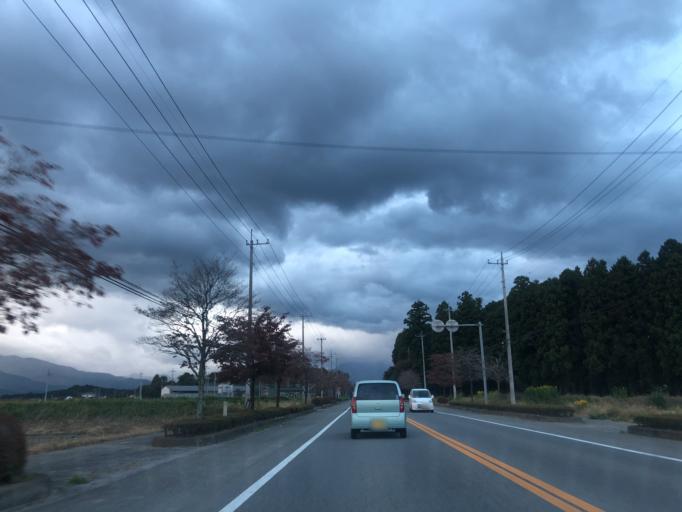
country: JP
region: Tochigi
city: Kuroiso
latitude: 36.9442
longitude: 140.0070
